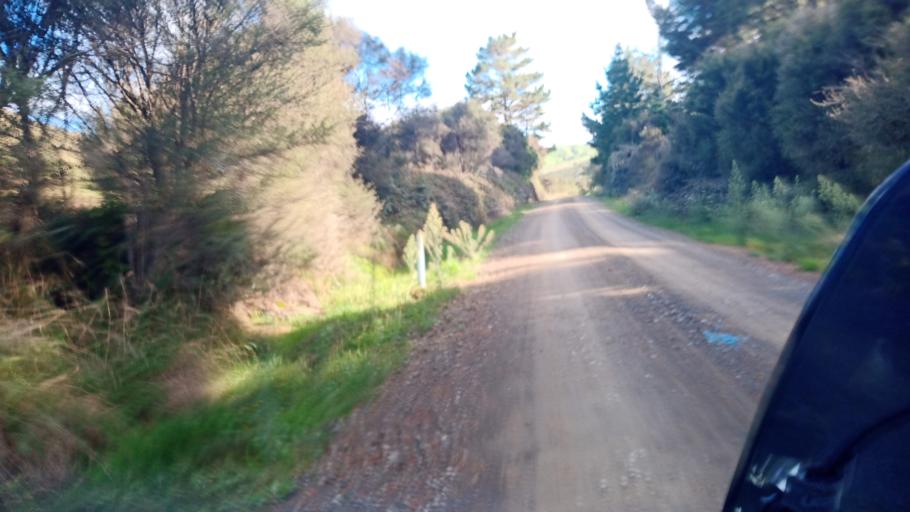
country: NZ
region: Bay of Plenty
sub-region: Opotiki District
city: Opotiki
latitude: -38.4609
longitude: 177.4194
